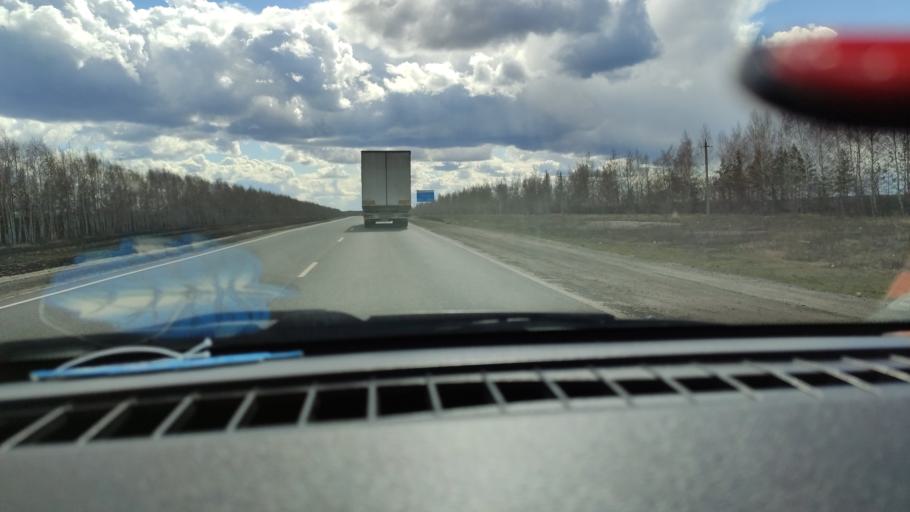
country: RU
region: Samara
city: Syzran'
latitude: 52.9910
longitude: 48.3216
